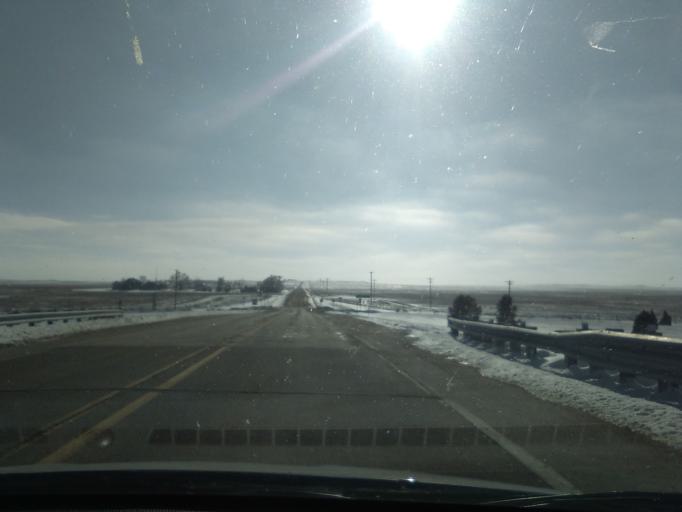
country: US
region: Wyoming
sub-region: Laramie County
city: Pine Bluffs
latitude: 41.1916
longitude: -103.8931
